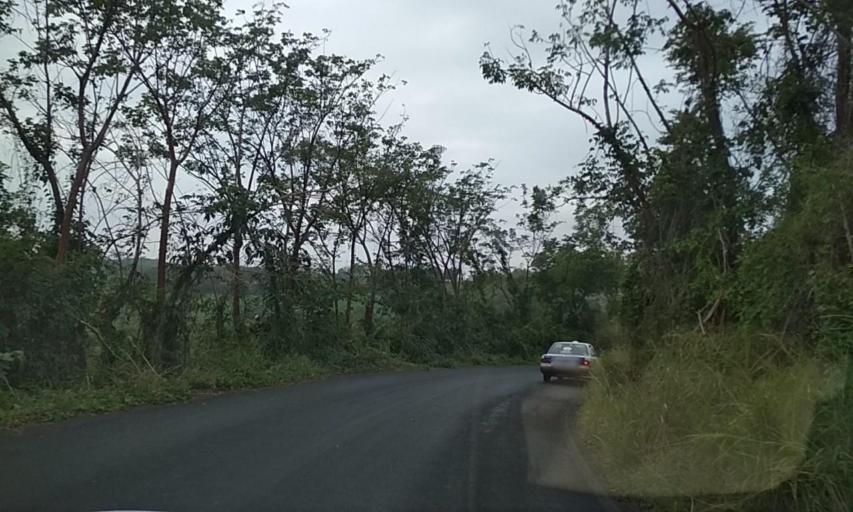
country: MX
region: Veracruz
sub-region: Coatzintla
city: Manuel Maria Contreras
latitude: 20.4466
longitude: -97.4950
